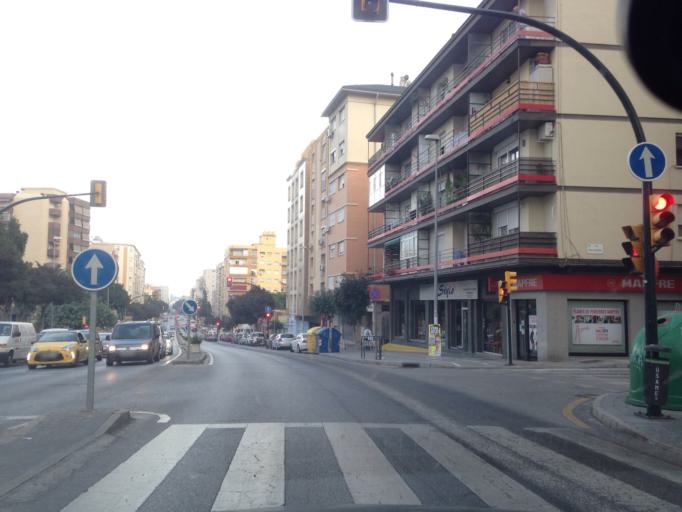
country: ES
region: Andalusia
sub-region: Provincia de Malaga
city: Malaga
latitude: 36.7215
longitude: -4.4438
